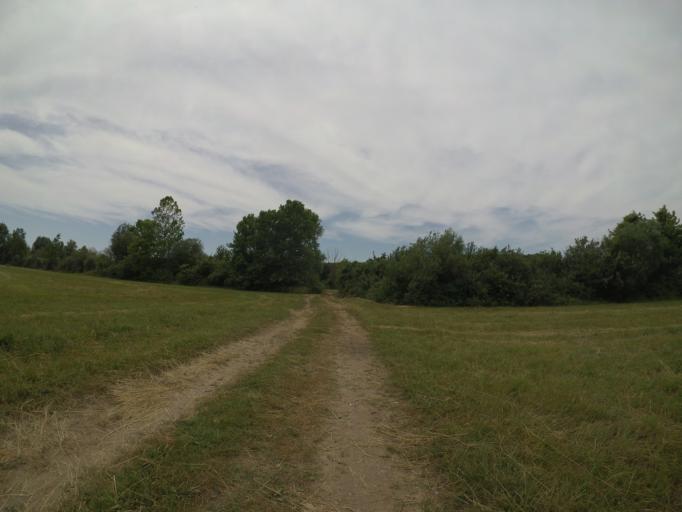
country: IT
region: Friuli Venezia Giulia
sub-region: Provincia di Udine
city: Bertiolo
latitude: 45.9324
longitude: 13.0570
